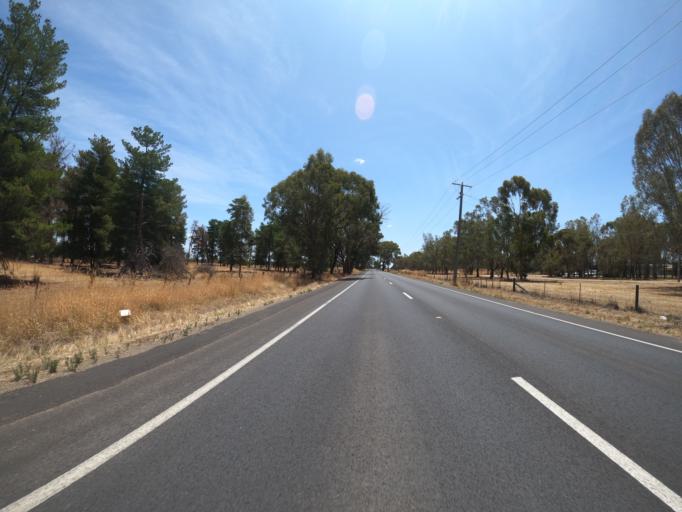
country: AU
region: Victoria
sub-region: Benalla
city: Benalla
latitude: -36.5262
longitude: 146.0385
